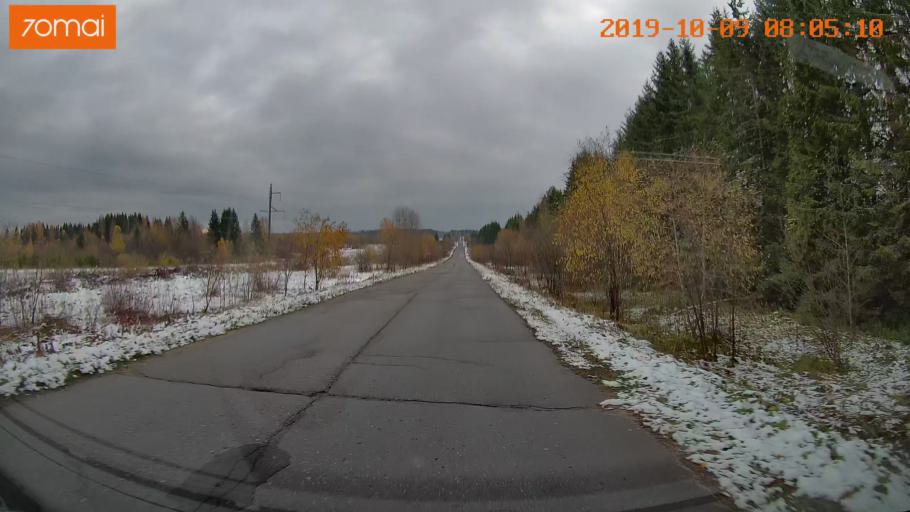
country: RU
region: Jaroslavl
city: Kukoboy
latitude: 58.6906
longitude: 40.0389
